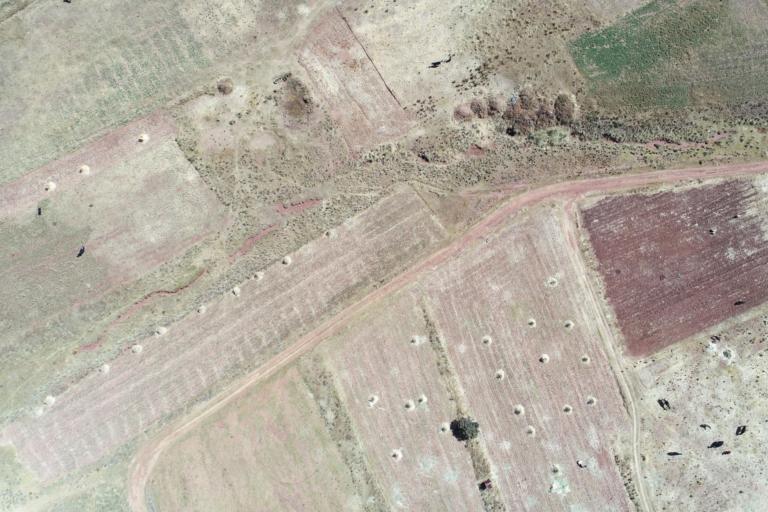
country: BO
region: La Paz
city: Tiahuanaco
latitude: -16.6015
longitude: -68.7727
